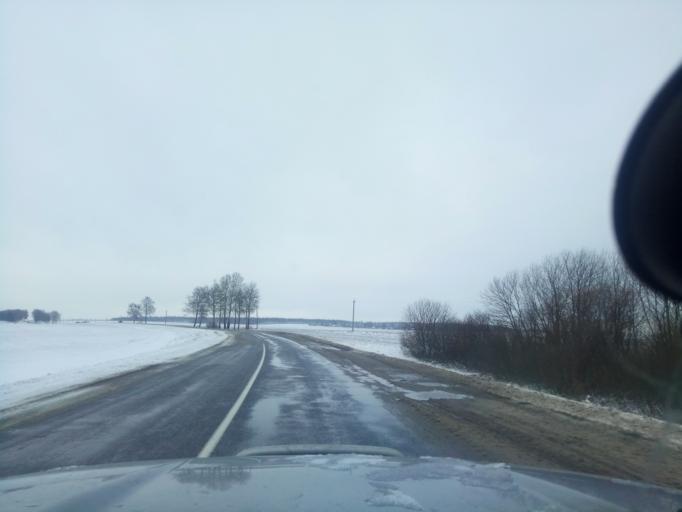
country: BY
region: Minsk
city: Kapyl'
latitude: 53.0999
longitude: 27.0524
